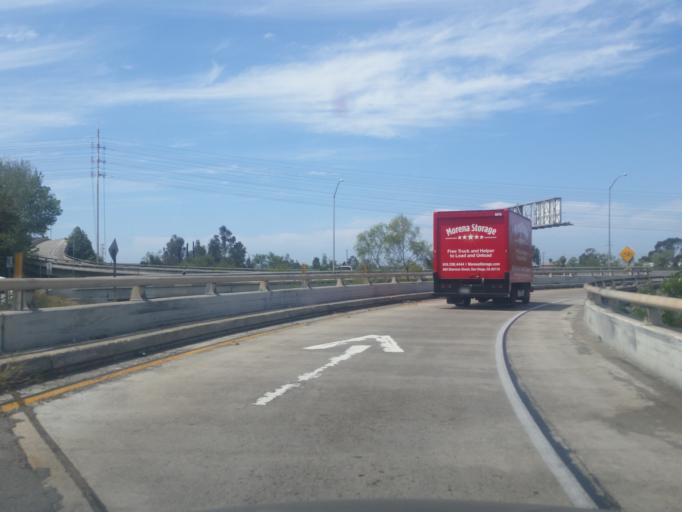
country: US
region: California
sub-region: San Diego County
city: San Diego
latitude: 32.7608
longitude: -117.1972
